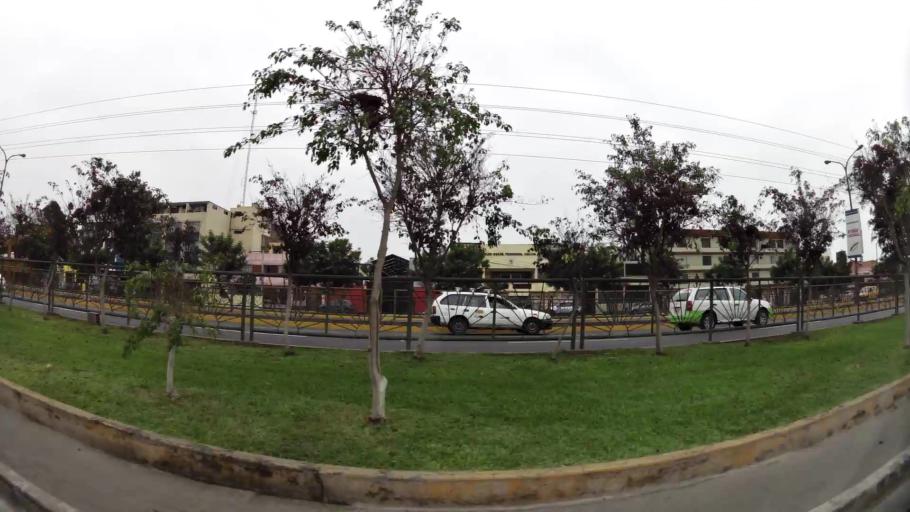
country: PE
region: Callao
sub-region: Callao
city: Callao
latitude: -12.0495
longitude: -77.0753
